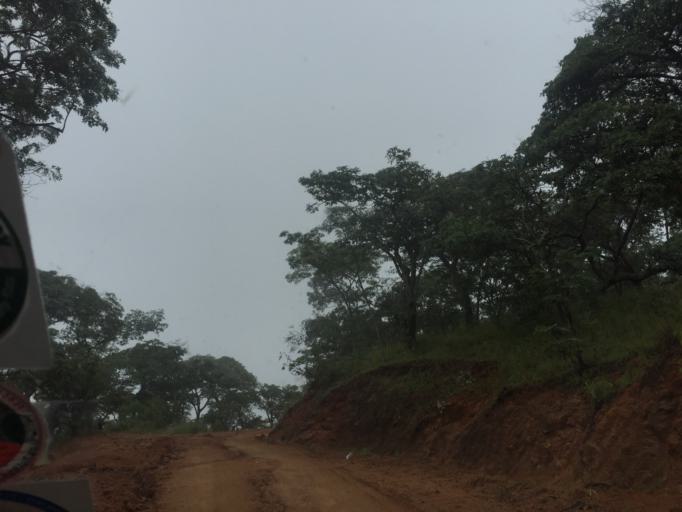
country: TZ
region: Mbeya
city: Chimala
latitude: -8.8700
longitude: 33.9939
